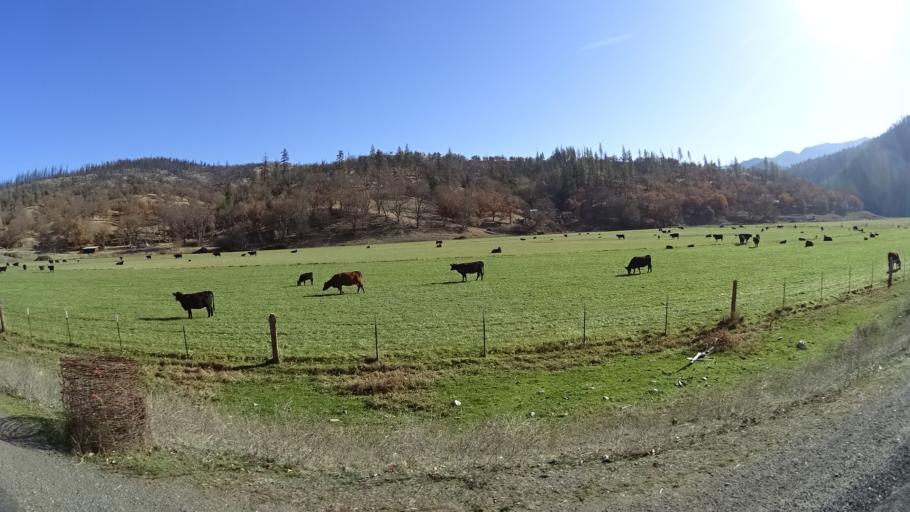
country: US
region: California
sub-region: Siskiyou County
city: Happy Camp
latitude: 41.8300
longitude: -123.0067
